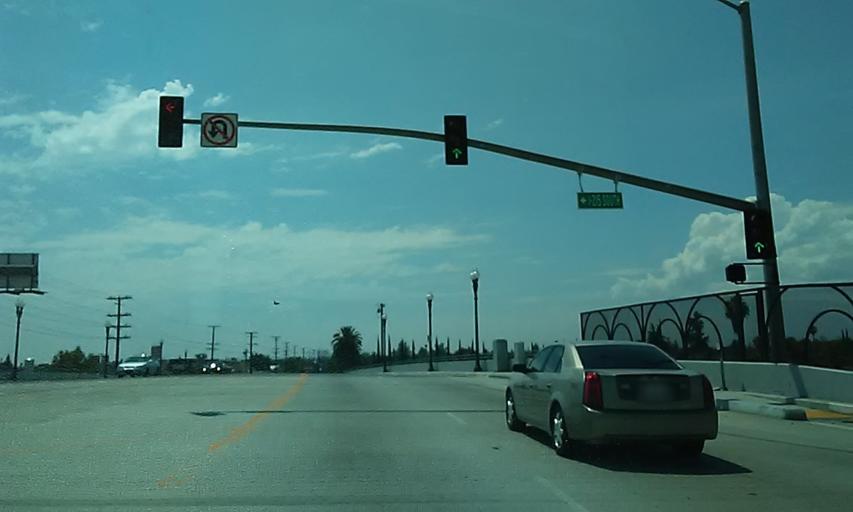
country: US
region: California
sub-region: San Bernardino County
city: San Bernardino
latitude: 34.1216
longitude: -117.3030
